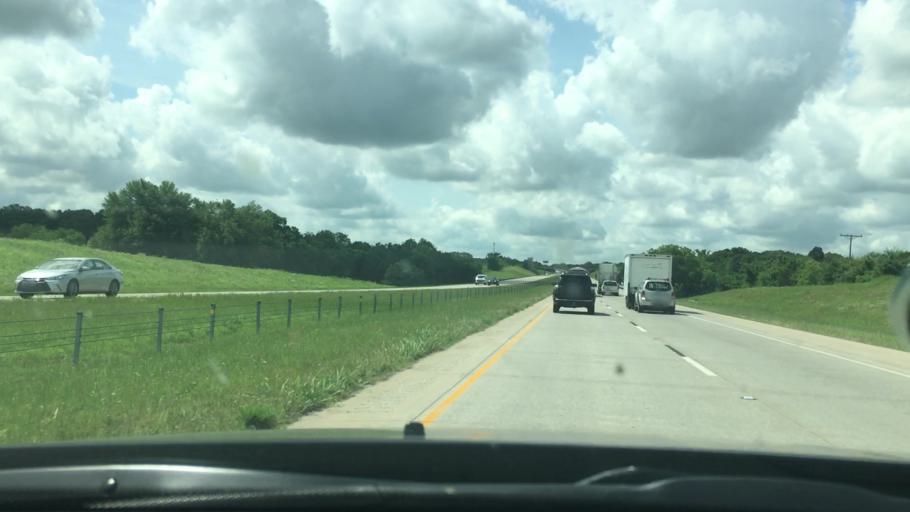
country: US
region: Oklahoma
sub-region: Love County
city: Marietta
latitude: 33.8602
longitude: -97.1343
